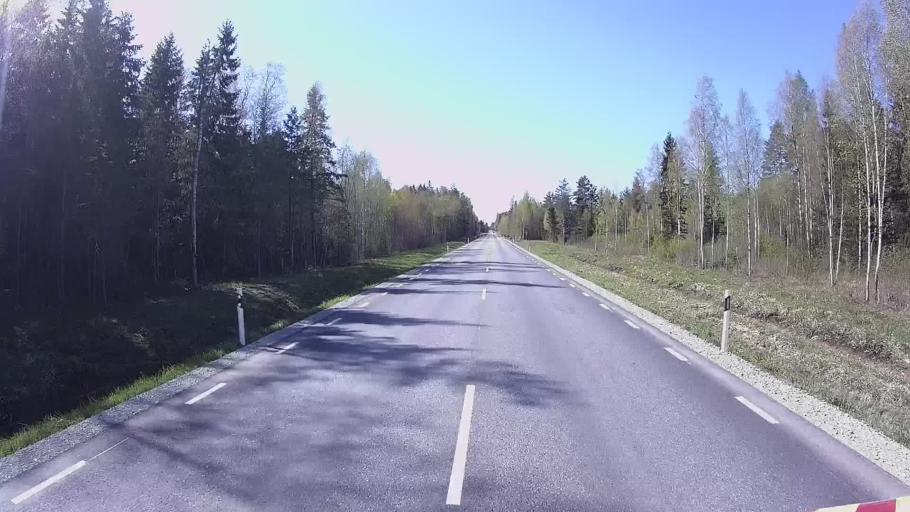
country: EE
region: Raplamaa
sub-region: Jaervakandi vald
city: Jarvakandi
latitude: 58.7308
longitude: 24.8027
